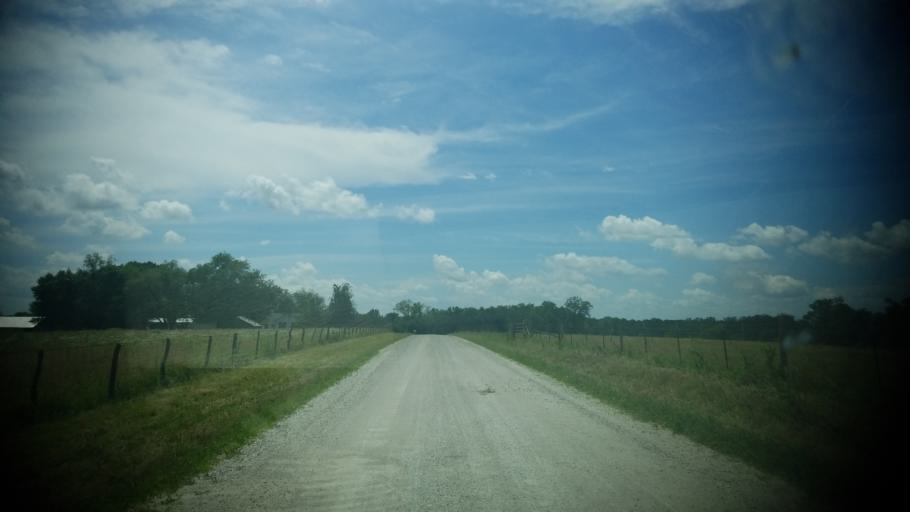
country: US
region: Missouri
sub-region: Audrain County
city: Vandalia
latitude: 39.3091
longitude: -91.3416
